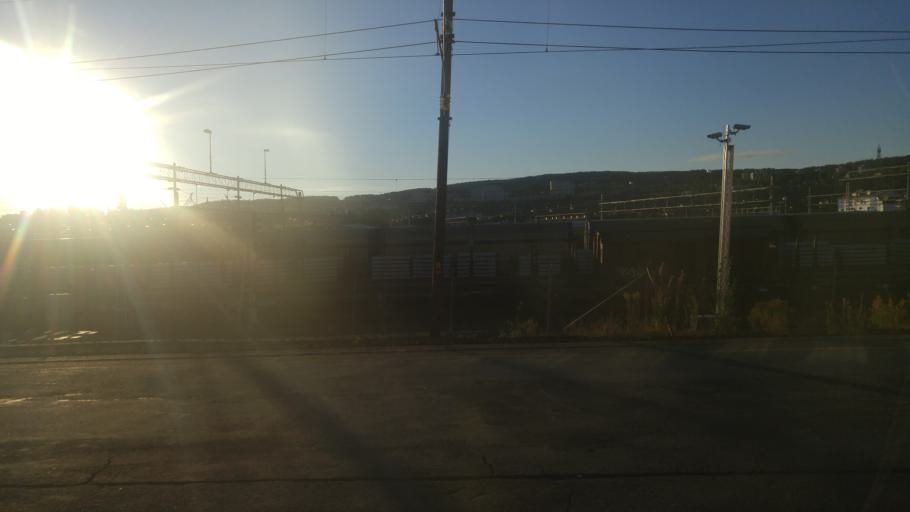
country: NO
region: Oslo
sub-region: Oslo
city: Oslo
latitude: 59.9319
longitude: 10.8348
